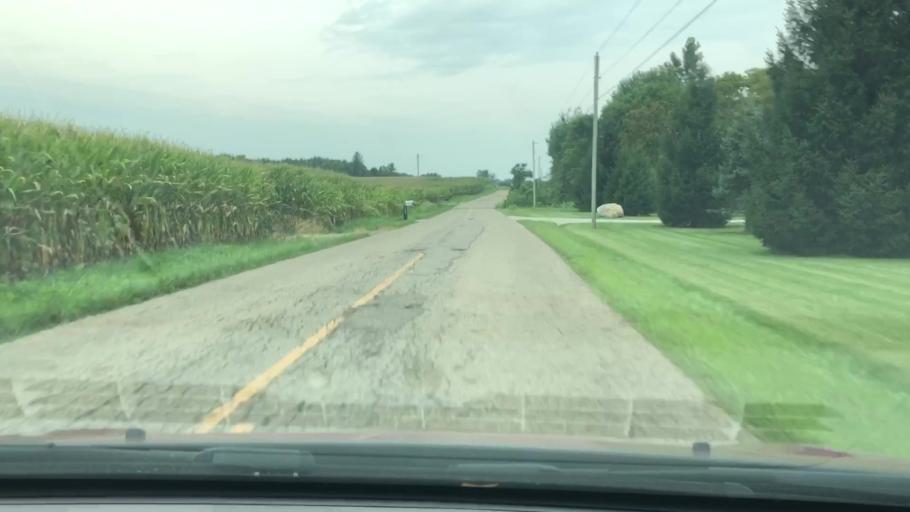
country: US
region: Ohio
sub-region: Knox County
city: Centerburg
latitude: 40.3299
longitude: -82.7270
